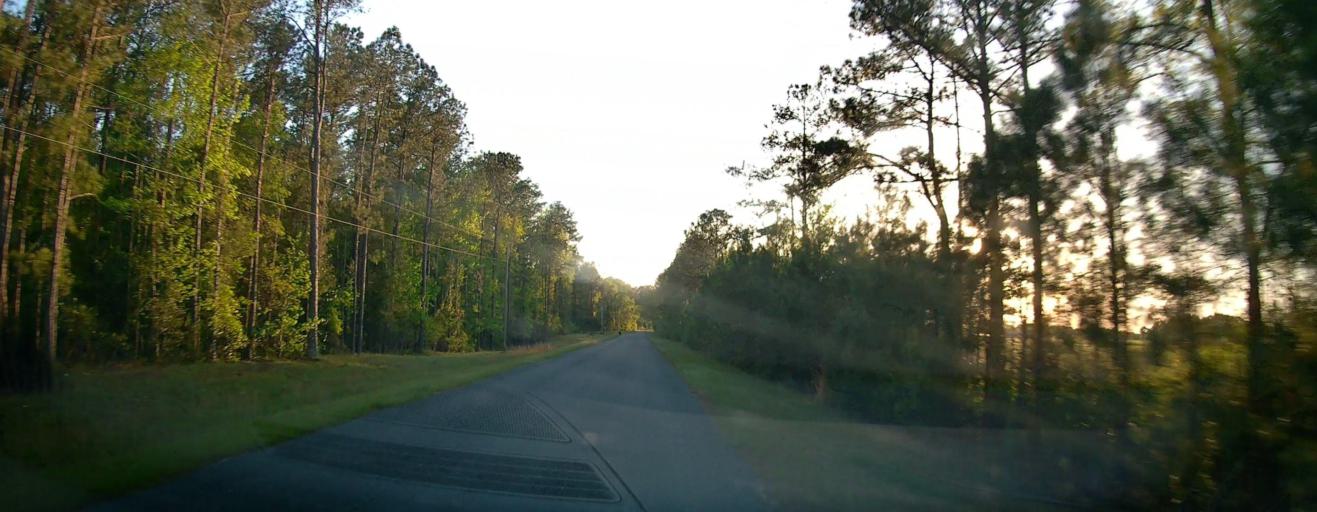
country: US
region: Georgia
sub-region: Talbot County
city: Talbotton
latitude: 32.5360
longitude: -84.5918
